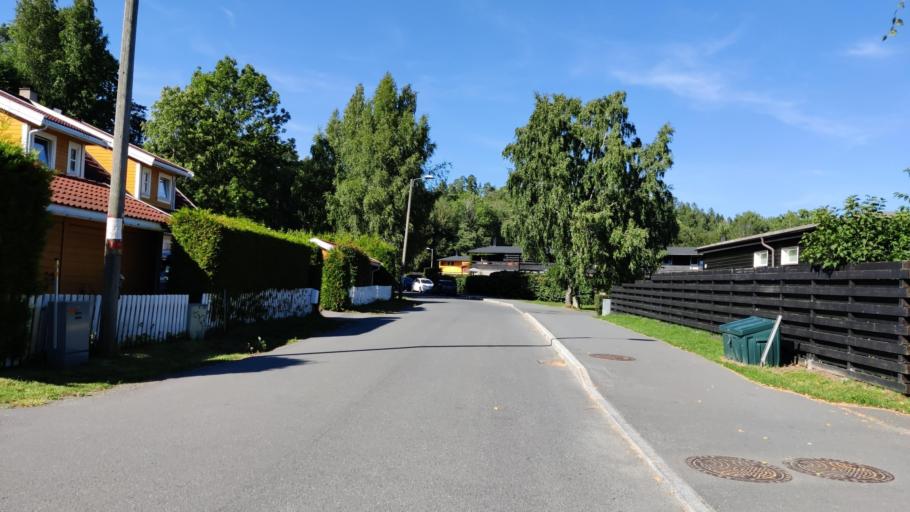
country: NO
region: Akershus
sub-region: Baerum
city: Lysaker
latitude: 59.9309
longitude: 10.6033
